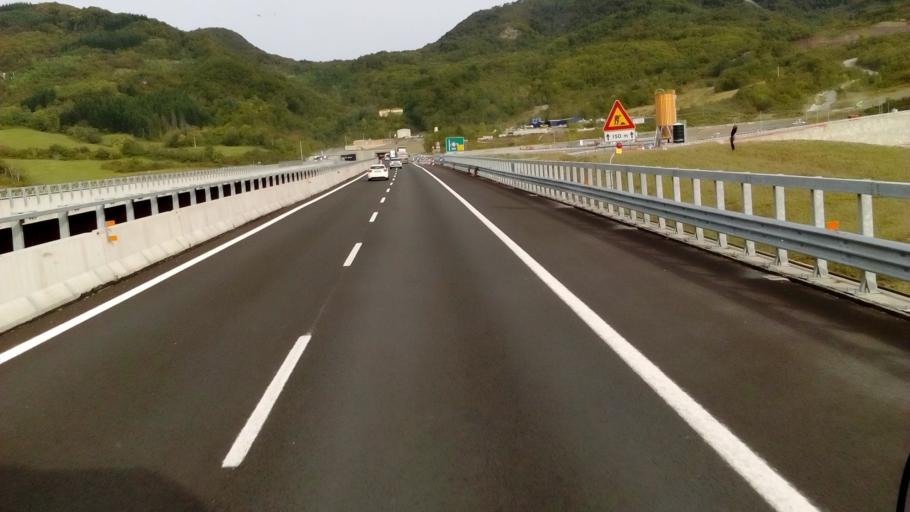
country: IT
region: Tuscany
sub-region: Province of Florence
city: Barberino di Mugello
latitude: 44.0663
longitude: 11.2430
